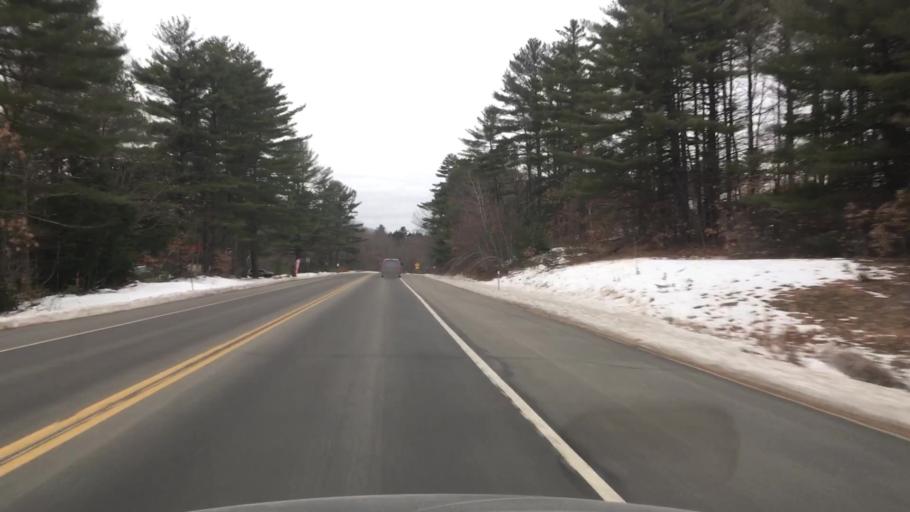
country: US
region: New Hampshire
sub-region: Merrimack County
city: Sutton
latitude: 43.2656
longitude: -71.9545
